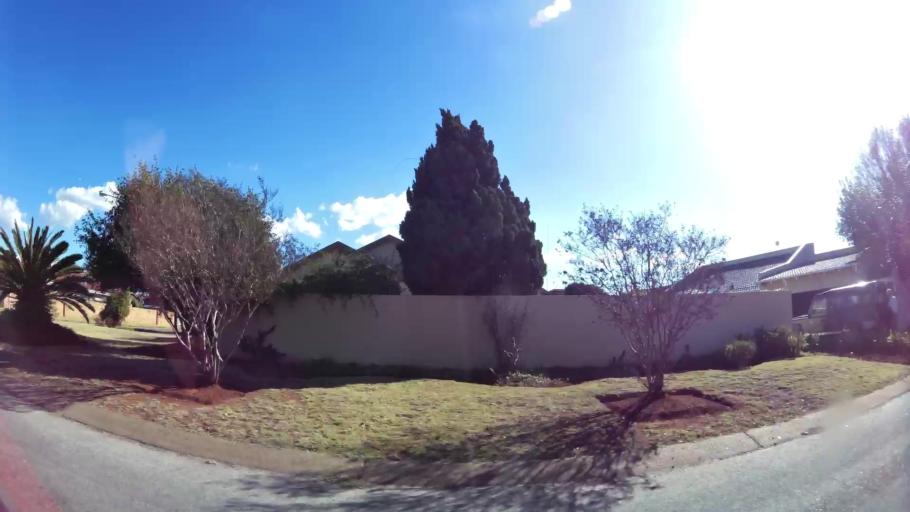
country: ZA
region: Gauteng
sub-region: West Rand District Municipality
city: Carletonville
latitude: -26.3652
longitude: 27.3662
